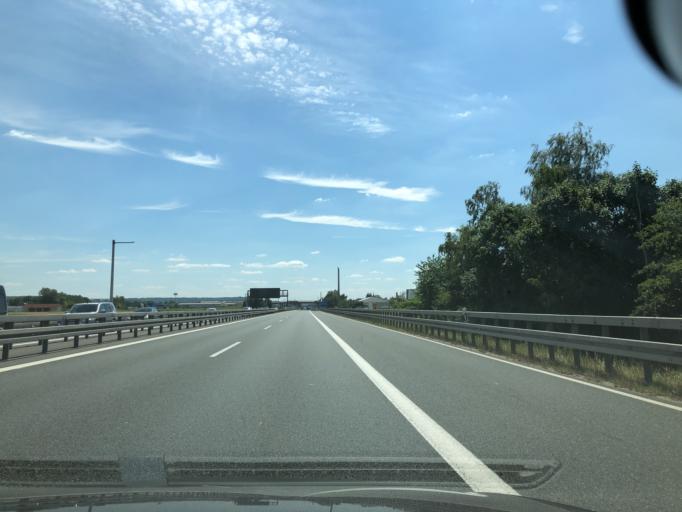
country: DE
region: Bavaria
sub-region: Regierungsbezirk Mittelfranken
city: Baiersdorf
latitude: 49.6727
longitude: 11.0468
